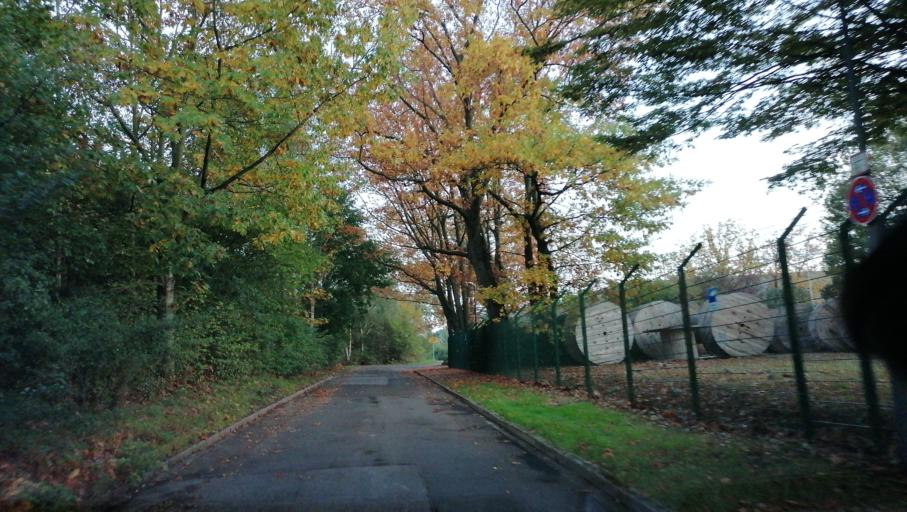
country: DE
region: North Rhine-Westphalia
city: Herten
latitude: 51.5768
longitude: 7.1666
